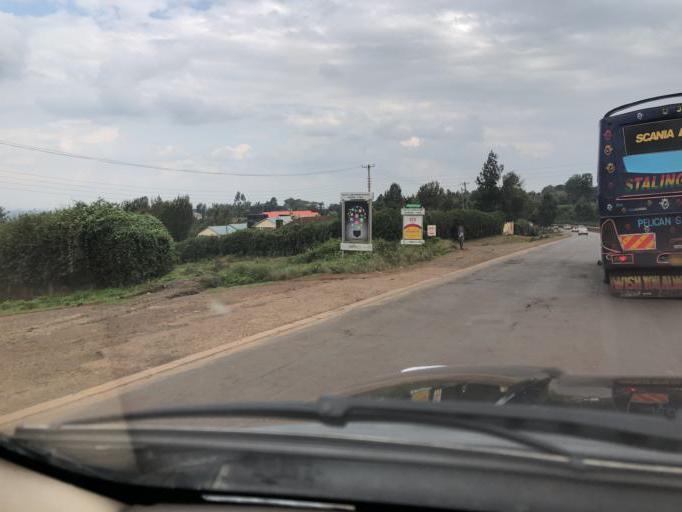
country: KE
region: Kiambu
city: Kikuyu
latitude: -1.2248
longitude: 36.6638
